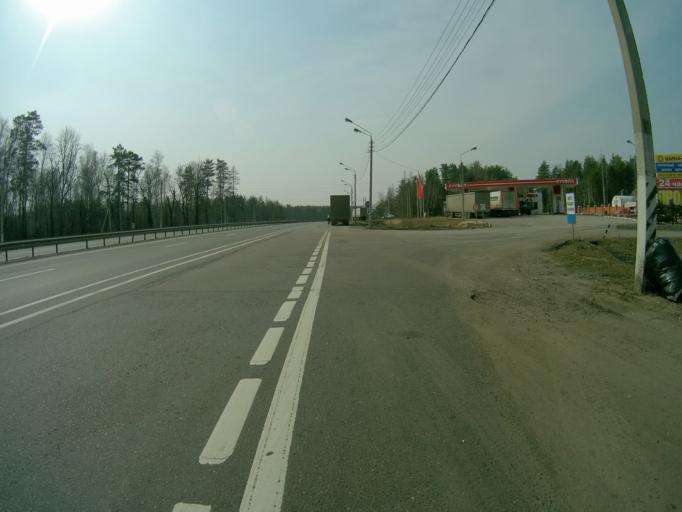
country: RU
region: Vladimir
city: Kommunar
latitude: 56.0624
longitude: 40.4549
